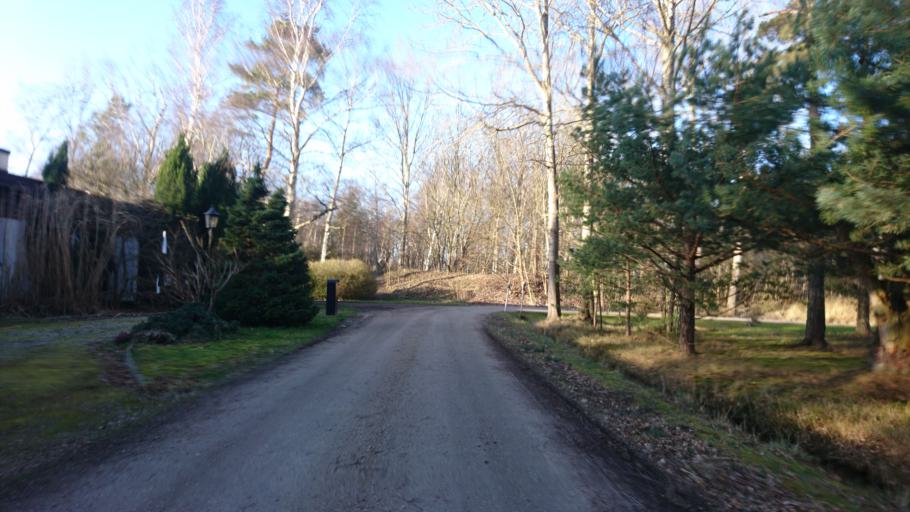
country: SE
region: Skane
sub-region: Vellinge Kommun
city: Ljunghusen
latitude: 55.4047
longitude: 12.9097
